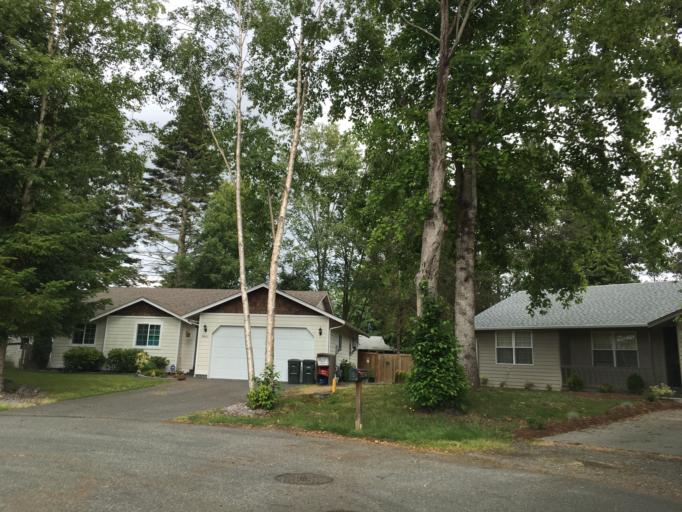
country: US
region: Washington
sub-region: Whatcom County
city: Birch Bay
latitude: 48.9481
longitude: -122.7447
